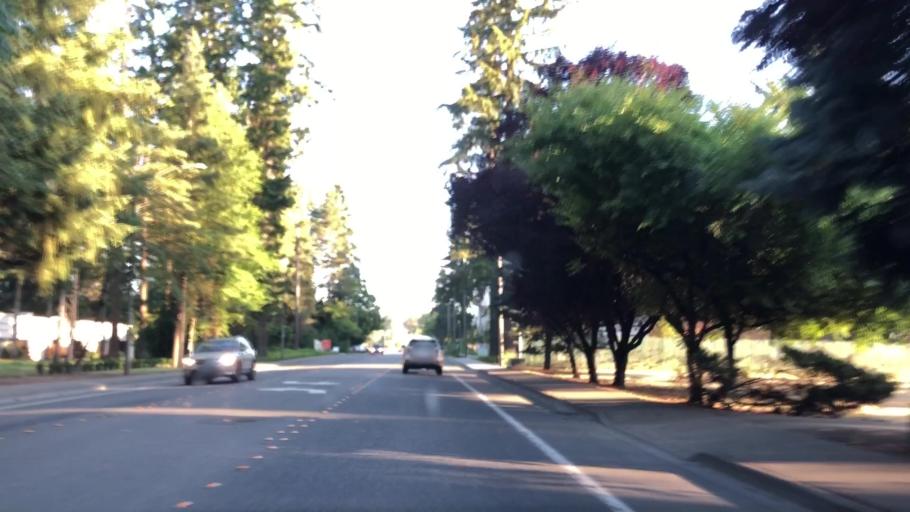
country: US
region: Washington
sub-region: King County
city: Redmond
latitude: 47.6696
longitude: -122.1001
